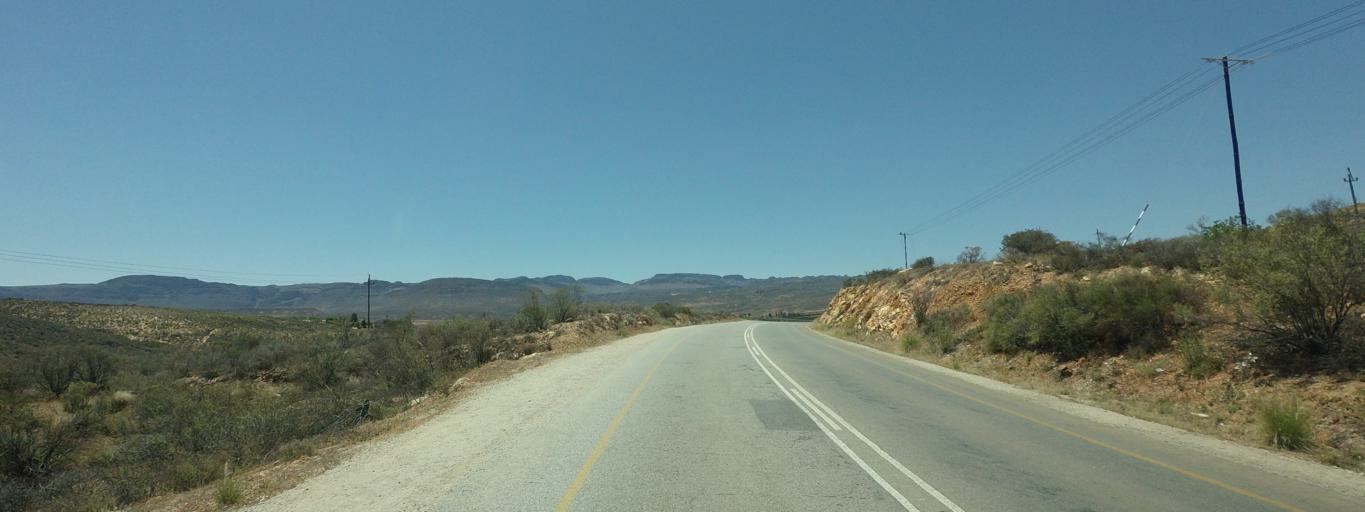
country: ZA
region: Western Cape
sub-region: West Coast District Municipality
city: Clanwilliam
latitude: -32.1709
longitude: 18.8735
